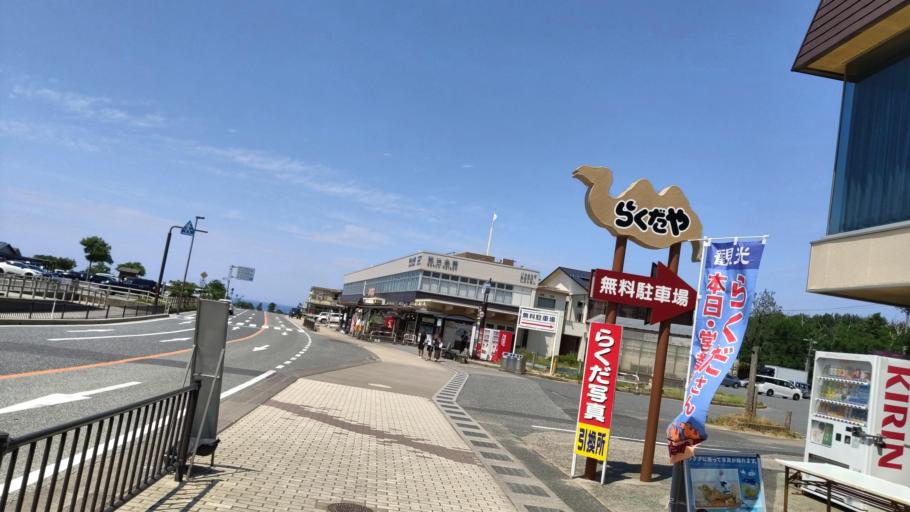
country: JP
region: Tottori
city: Tottori
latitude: 35.5431
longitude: 134.2369
